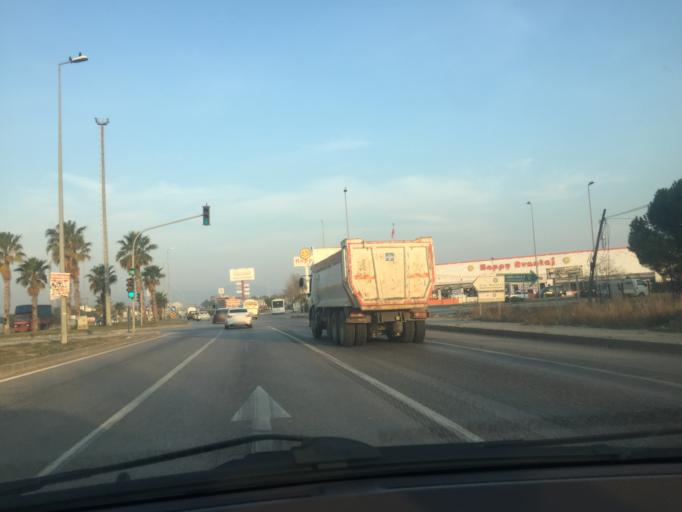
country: TR
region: Balikesir
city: Bandirma
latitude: 40.3236
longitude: 28.0044
